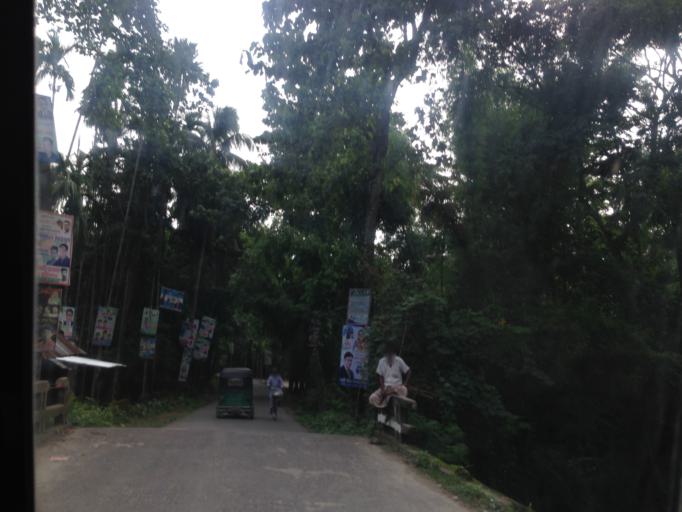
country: BD
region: Chittagong
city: Raipur
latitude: 23.0300
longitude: 90.7081
